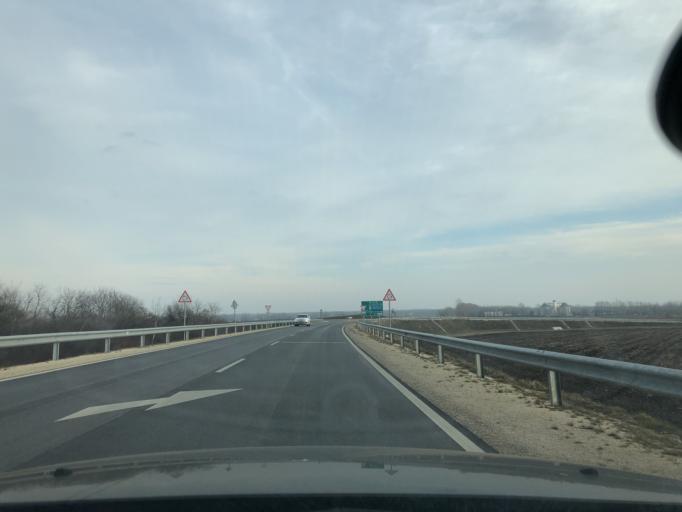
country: HU
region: Gyor-Moson-Sopron
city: Gyor
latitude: 47.7373
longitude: 17.6718
